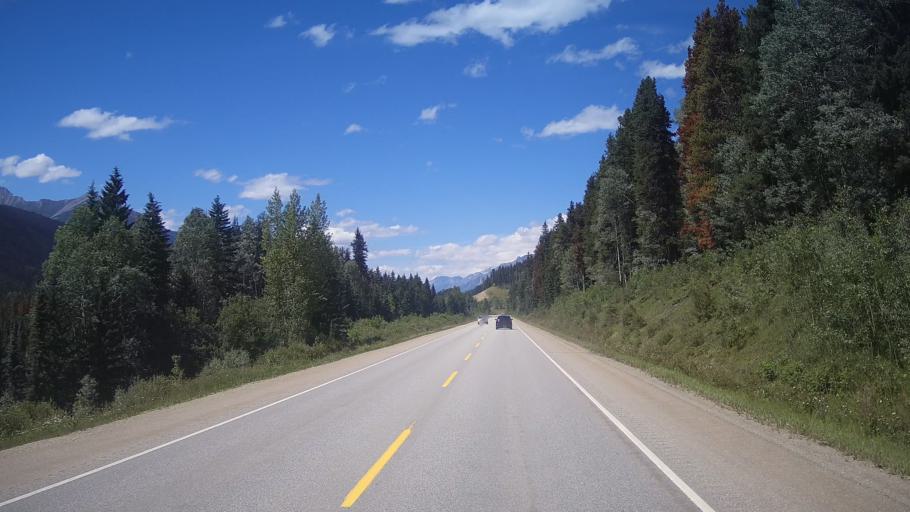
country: CA
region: Alberta
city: Jasper Park Lodge
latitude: 52.8750
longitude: -118.6906
